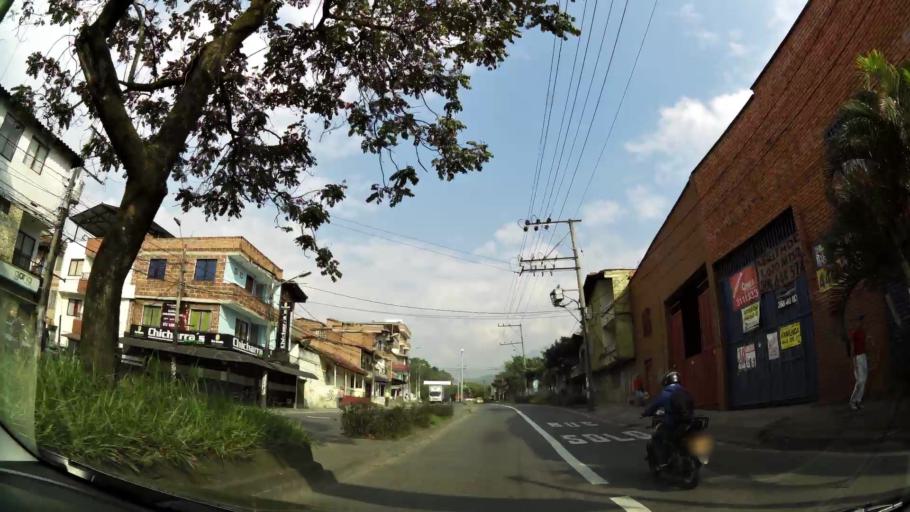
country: CO
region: Antioquia
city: Sabaneta
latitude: 6.1677
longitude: -75.6210
